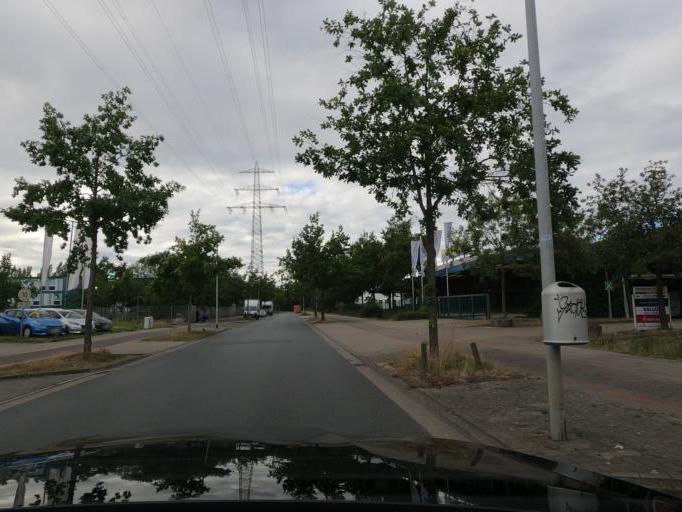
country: DE
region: Lower Saxony
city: Isernhagen Farster Bauerschaft
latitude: 52.4203
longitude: 9.8311
